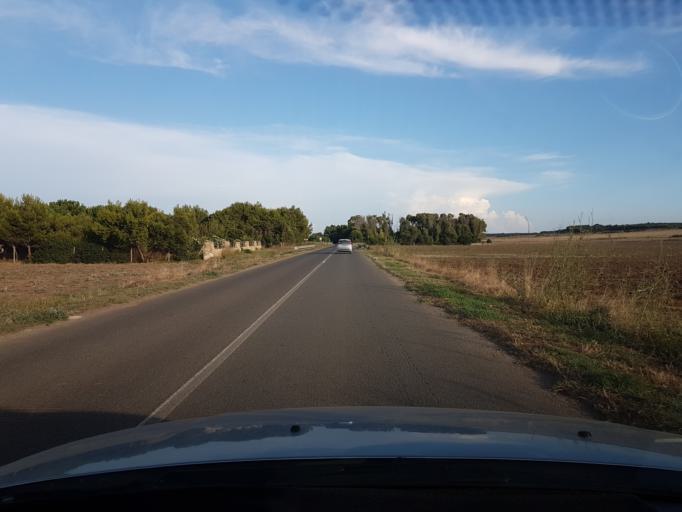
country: IT
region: Sardinia
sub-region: Provincia di Oristano
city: Cabras
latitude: 39.9483
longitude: 8.4297
